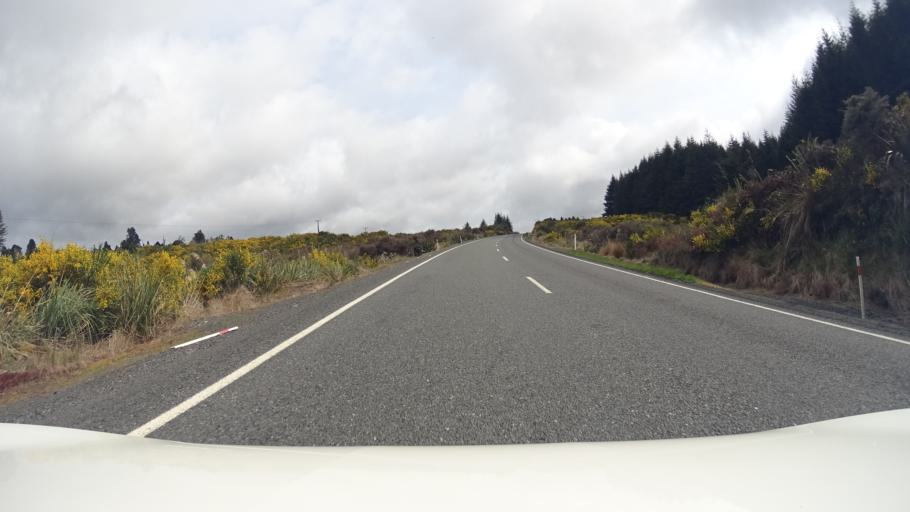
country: NZ
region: Manawatu-Wanganui
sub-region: Ruapehu District
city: Waiouru
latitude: -39.2010
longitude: 175.4013
